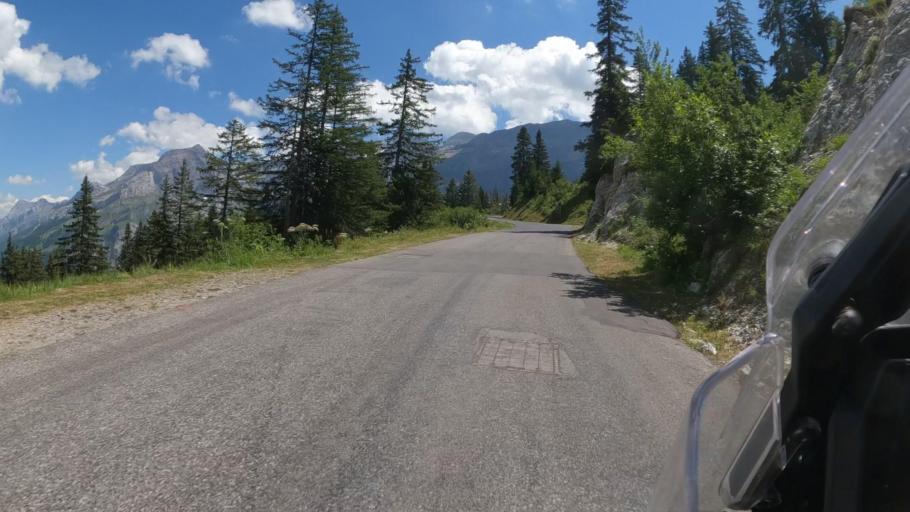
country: CH
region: Vaud
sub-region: Aigle District
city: Villars-sur-Ollon
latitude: 46.3265
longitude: 7.1252
